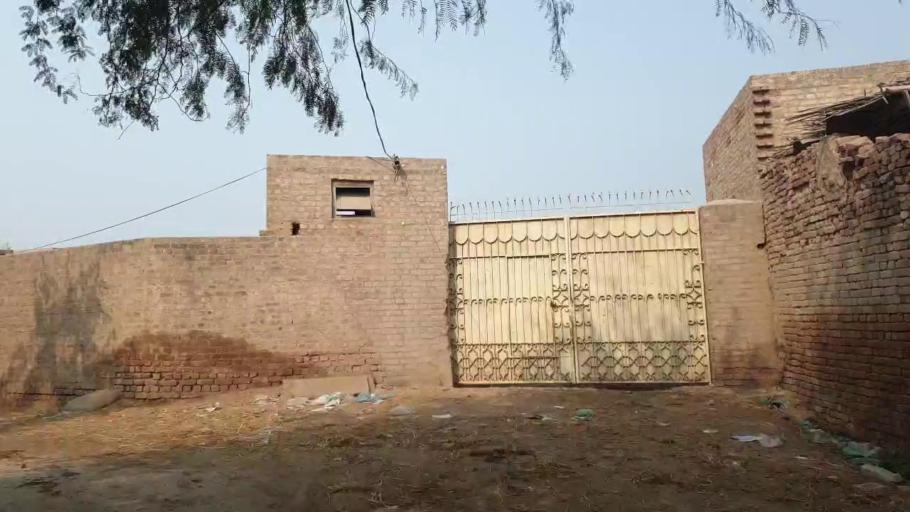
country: PK
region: Sindh
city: Tando Muhammad Khan
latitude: 25.1976
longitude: 68.5658
